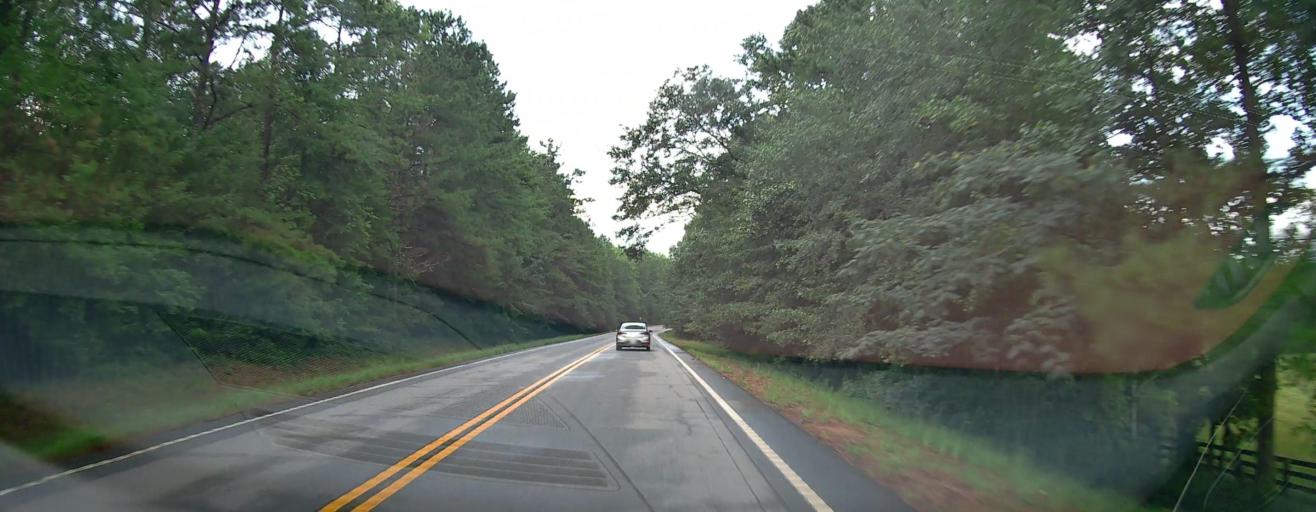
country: US
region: Georgia
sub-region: Coweta County
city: Senoia
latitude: 33.2668
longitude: -84.5549
